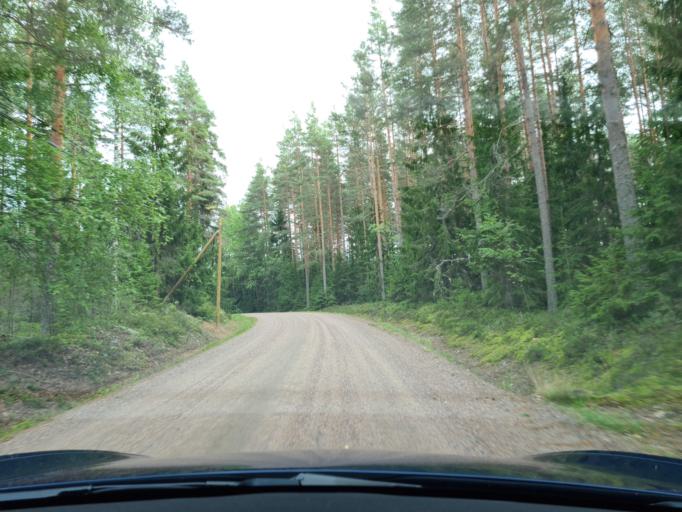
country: FI
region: Uusimaa
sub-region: Helsinki
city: Vihti
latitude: 60.4209
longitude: 24.4780
